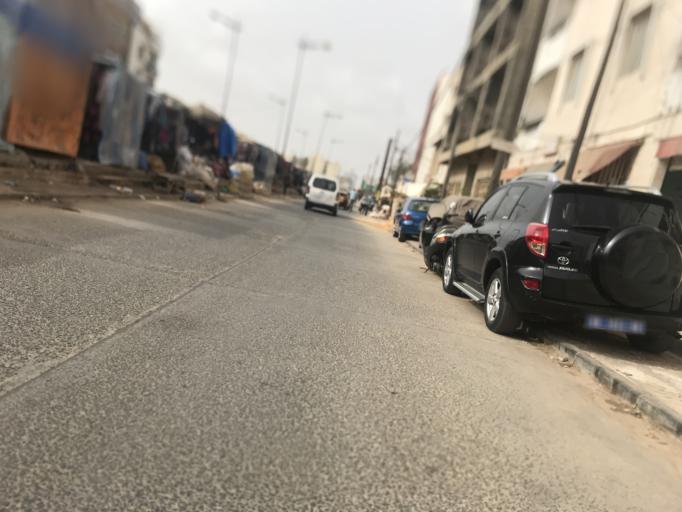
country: SN
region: Dakar
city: Dakar
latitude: 14.6832
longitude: -17.4540
